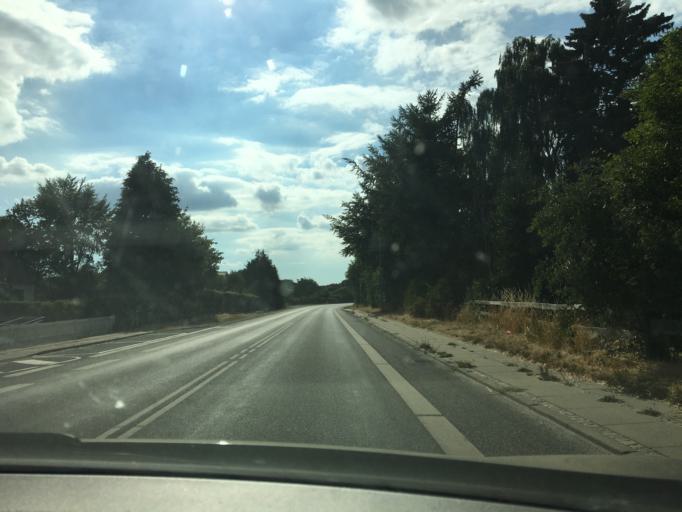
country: DK
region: South Denmark
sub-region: Nordfyns Kommune
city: Sonderso
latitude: 55.4199
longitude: 10.2671
